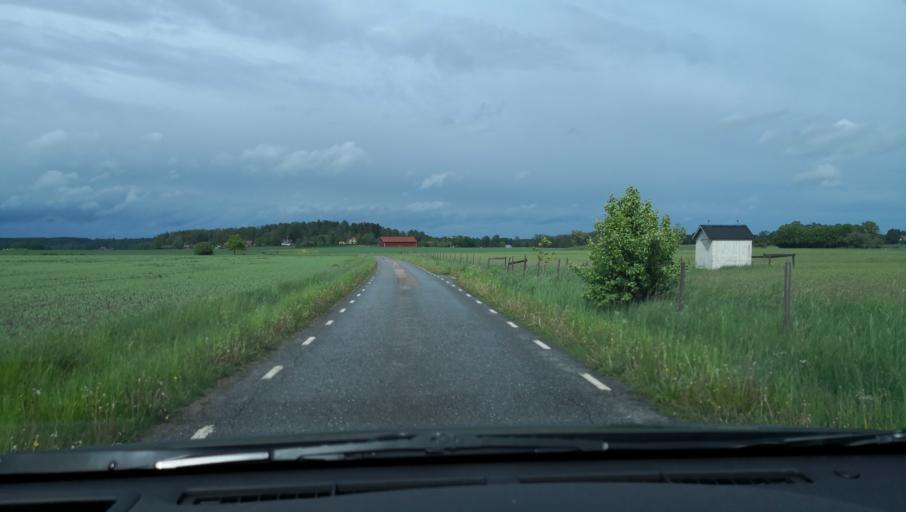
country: SE
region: Uppsala
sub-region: Enkopings Kommun
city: Orsundsbro
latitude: 59.7130
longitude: 17.4229
